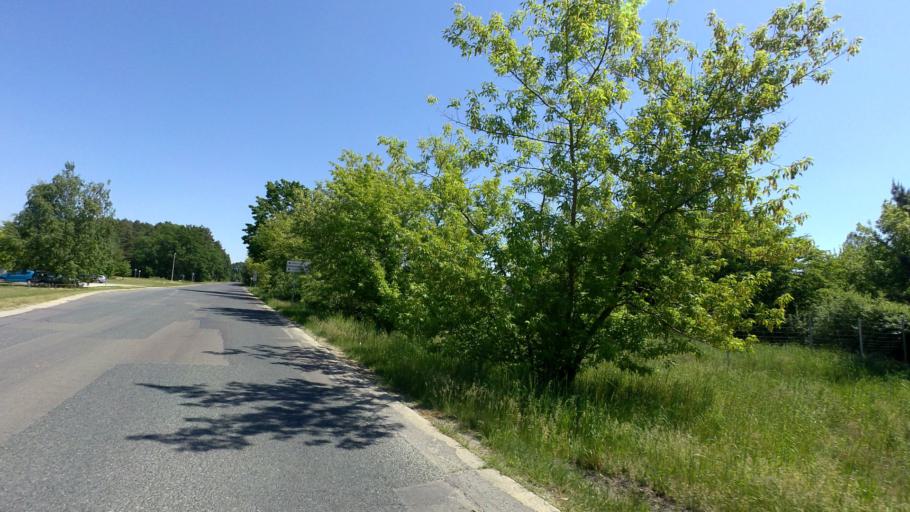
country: DE
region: Brandenburg
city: Cottbus
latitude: 51.7930
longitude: 14.3538
